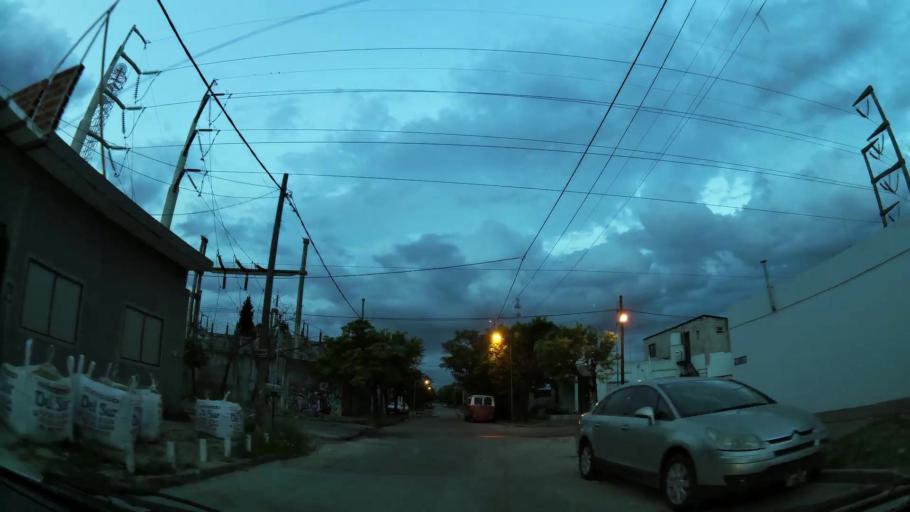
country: AR
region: Buenos Aires
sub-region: Partido de Quilmes
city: Quilmes
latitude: -34.7454
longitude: -58.2340
